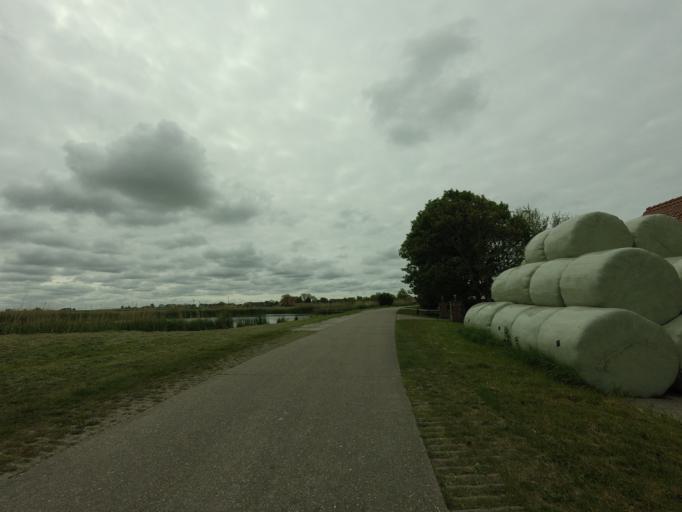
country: NL
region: Friesland
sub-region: Sudwest Fryslan
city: Workum
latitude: 52.9865
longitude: 5.4571
